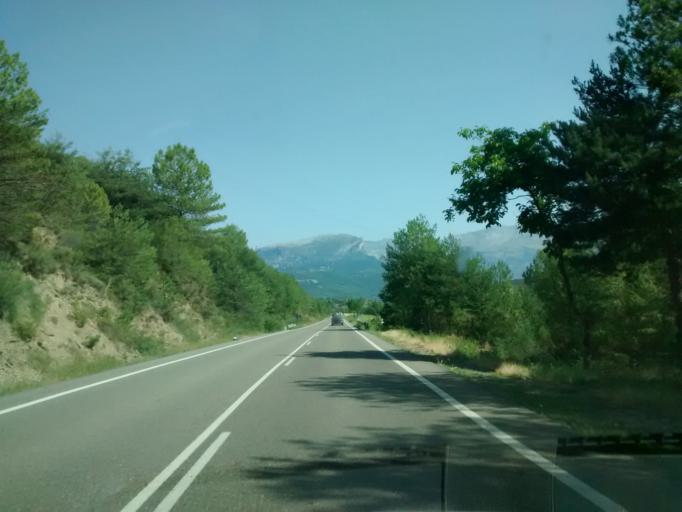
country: ES
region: Aragon
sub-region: Provincia de Huesca
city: Laspuna
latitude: 42.4870
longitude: 0.1476
